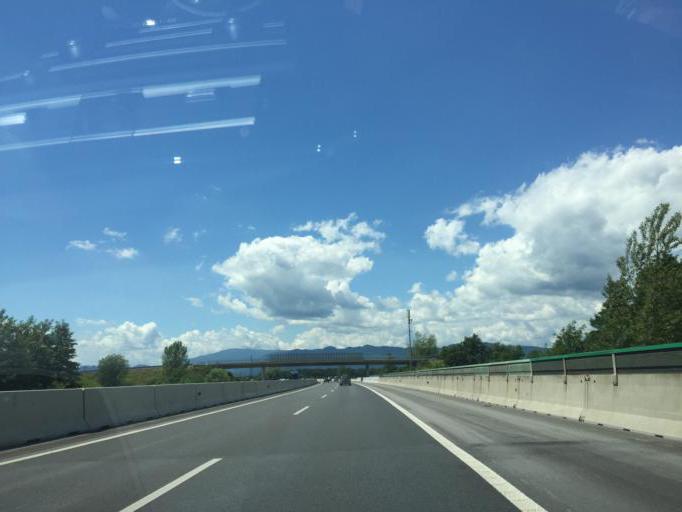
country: SI
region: Zalec
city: Gotovlje
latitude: 46.2717
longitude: 15.1352
